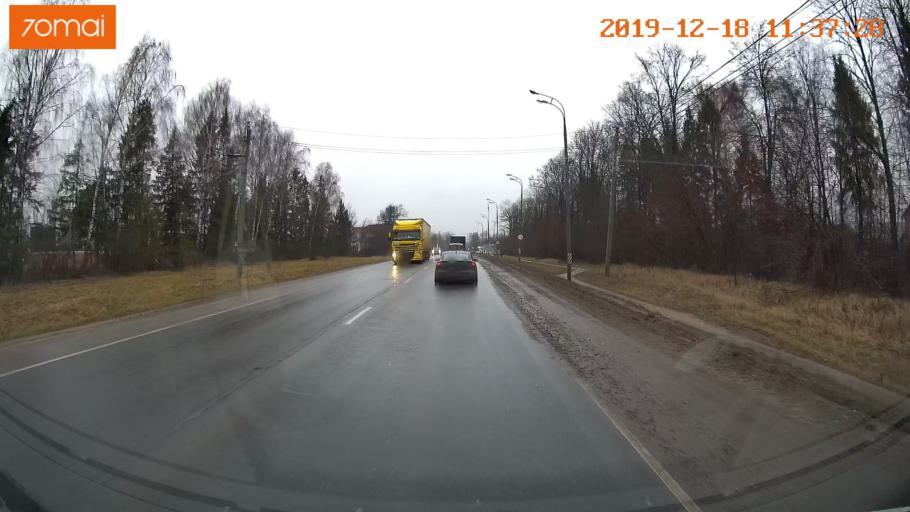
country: RU
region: Moskovskaya
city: Zvenigorod
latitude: 55.6905
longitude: 36.8951
